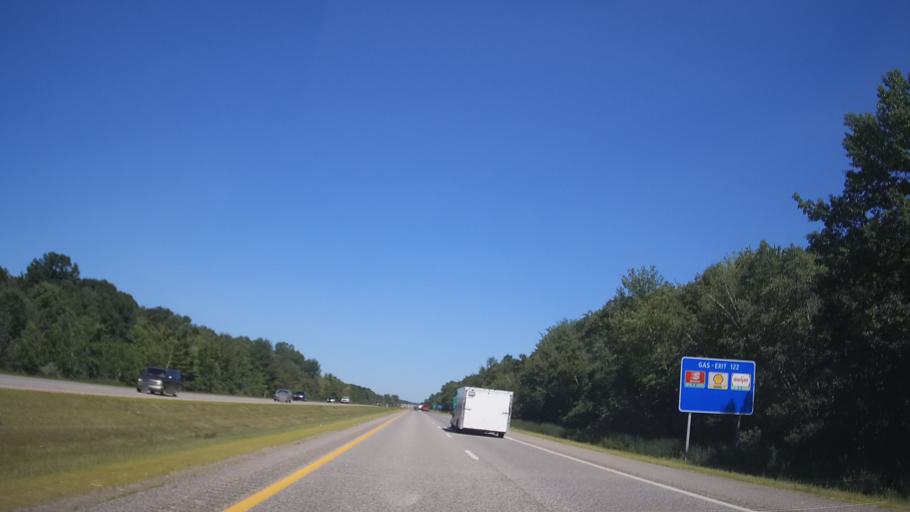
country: US
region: Michigan
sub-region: Midland County
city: Midland
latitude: 43.6561
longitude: -84.2888
